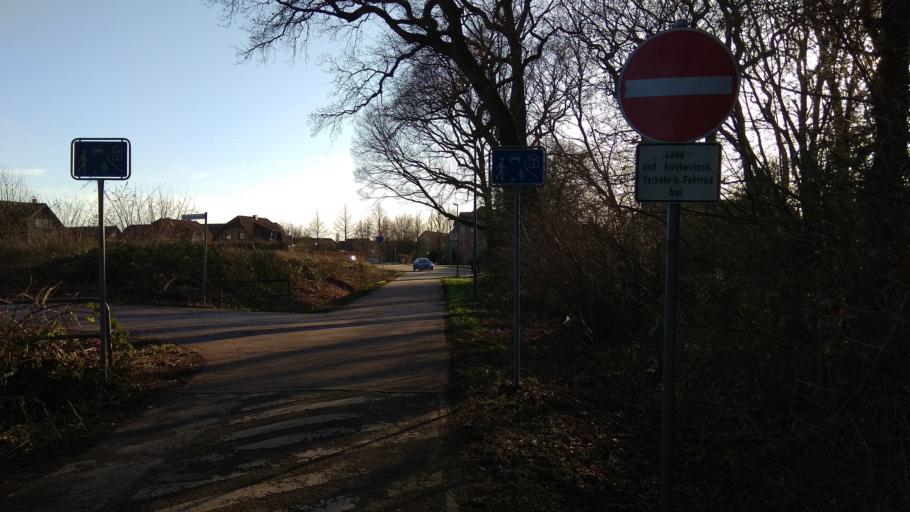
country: DE
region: North Rhine-Westphalia
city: Herten
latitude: 51.5943
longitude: 7.1741
